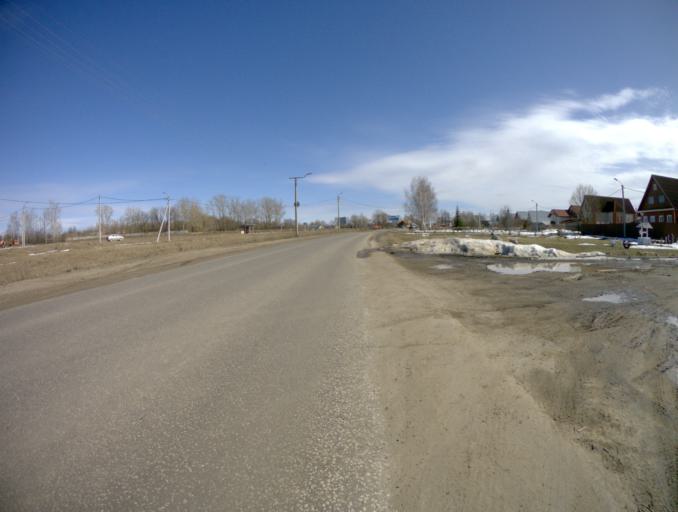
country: RU
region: Vladimir
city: Suzdal'
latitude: 56.4375
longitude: 40.4380
